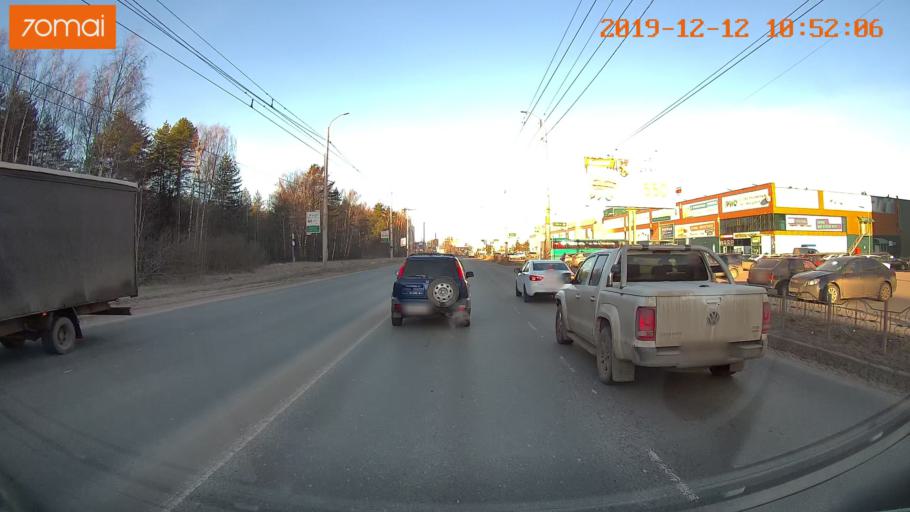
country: RU
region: Ivanovo
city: Kokhma
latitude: 56.9549
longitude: 41.0417
